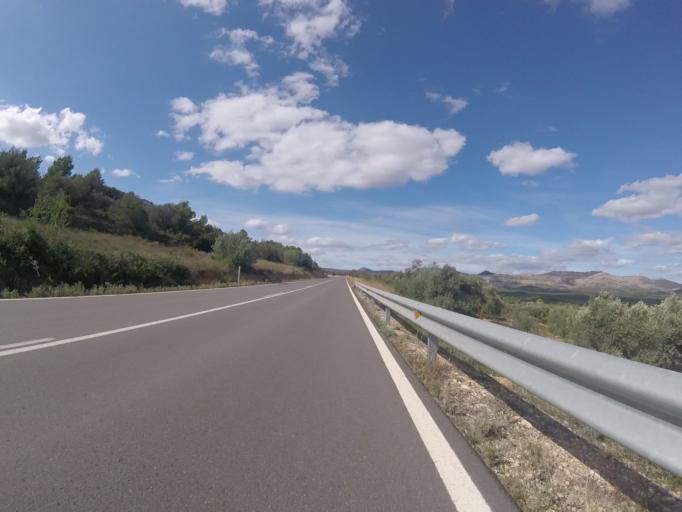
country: ES
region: Valencia
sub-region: Provincia de Castello
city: Chert/Xert
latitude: 40.4378
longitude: 0.1257
